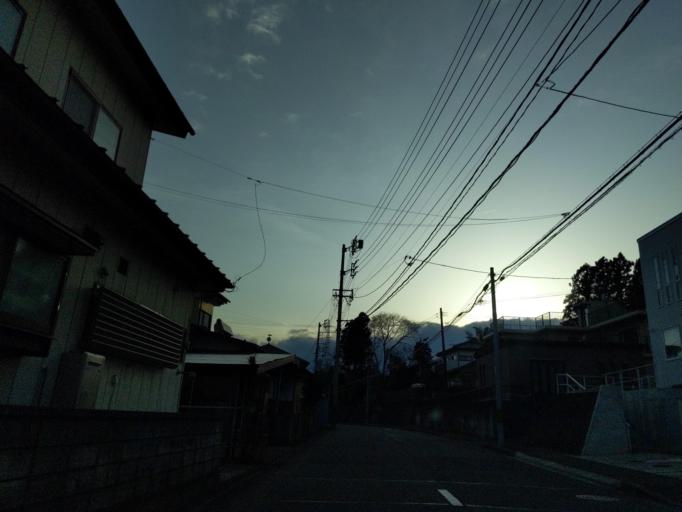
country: JP
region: Miyagi
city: Sendai
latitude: 38.2143
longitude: 140.8511
